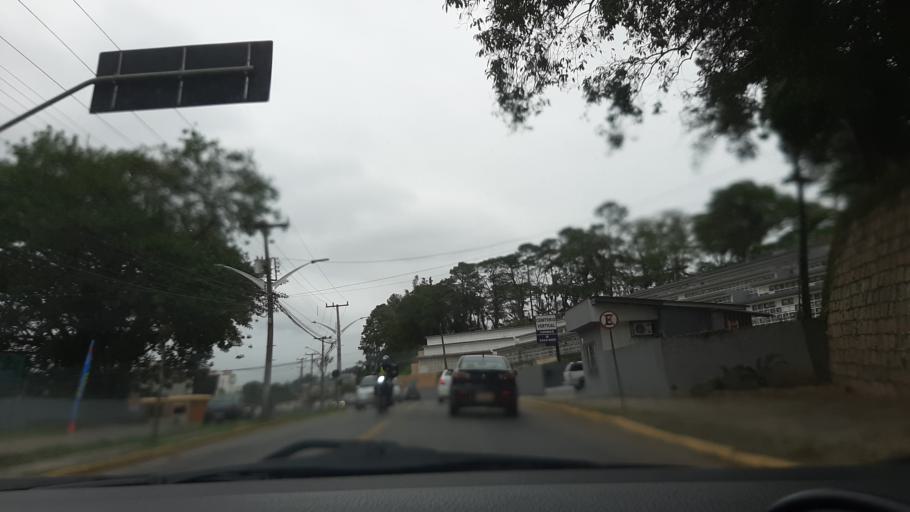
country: BR
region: Santa Catarina
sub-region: Joinville
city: Joinville
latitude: -26.3121
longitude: -48.8570
